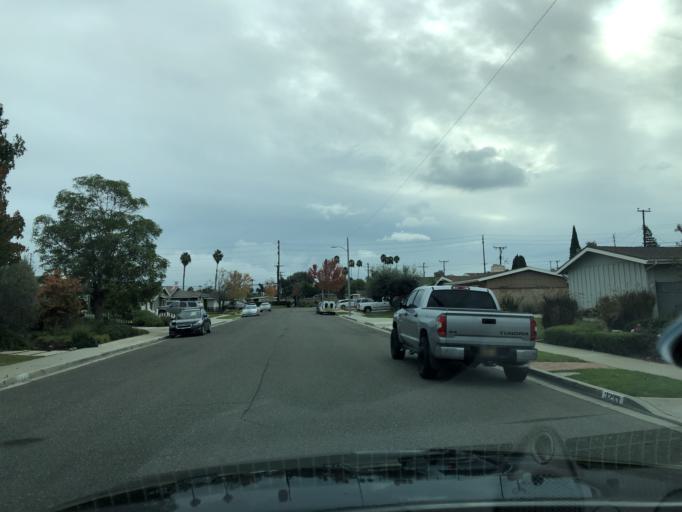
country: US
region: California
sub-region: Orange County
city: Fountain Valley
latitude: 33.6887
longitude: -117.9296
